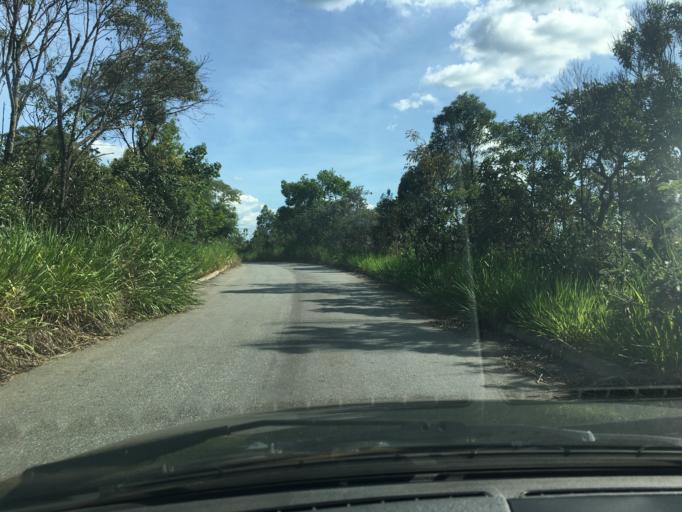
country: BR
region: Minas Gerais
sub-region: Ibirite
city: Ibirite
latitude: -20.1287
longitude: -44.0704
